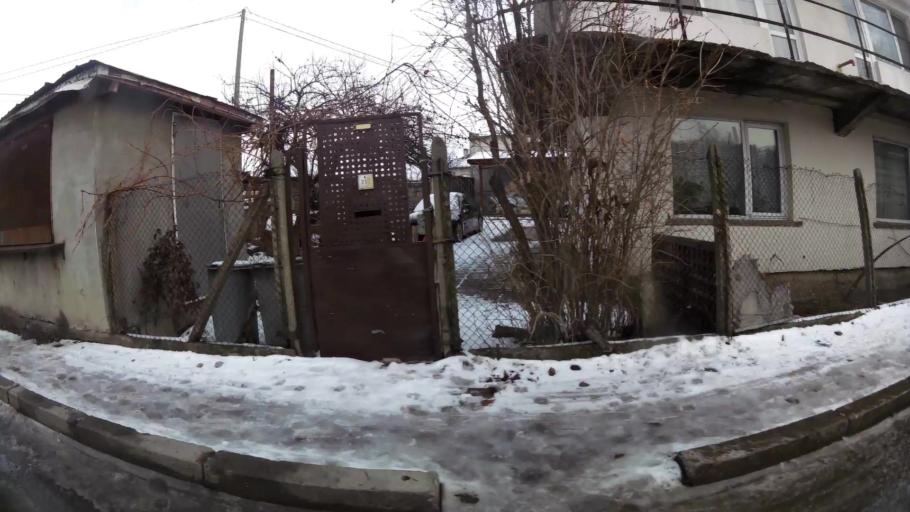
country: BG
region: Sofia-Capital
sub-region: Stolichna Obshtina
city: Sofia
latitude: 42.6882
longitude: 23.3841
